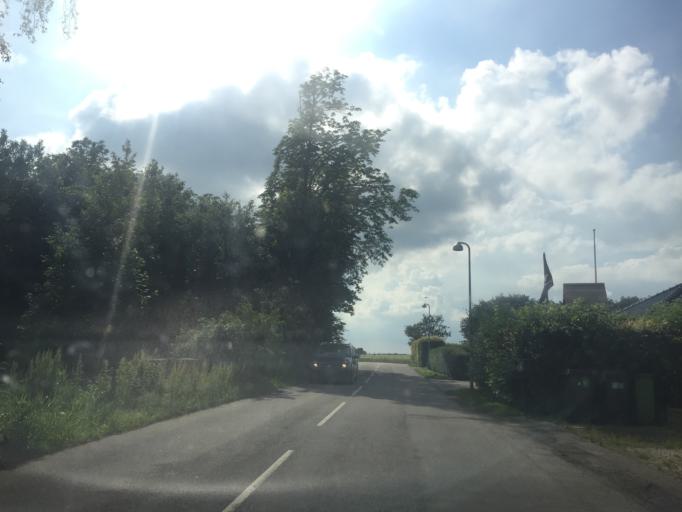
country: DK
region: Zealand
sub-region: Roskilde Kommune
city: Gundsomagle
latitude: 55.7100
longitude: 12.1597
